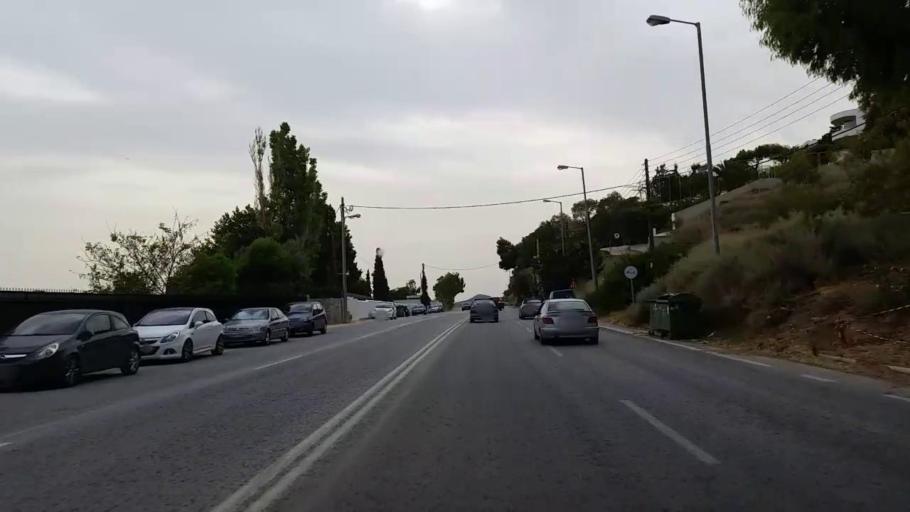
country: GR
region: Attica
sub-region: Nomarchia Anatolikis Attikis
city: Agios Dimitrios Kropias
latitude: 37.8041
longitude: 23.8574
